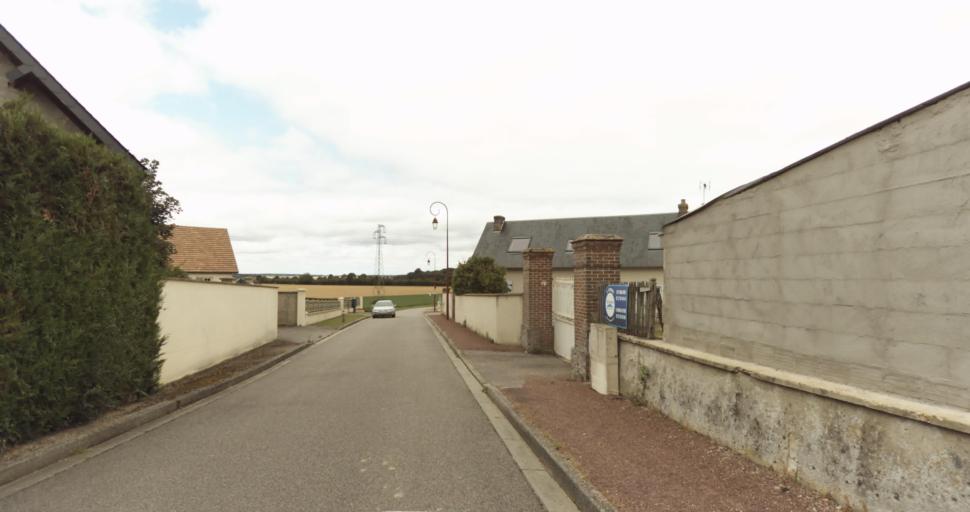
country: FR
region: Haute-Normandie
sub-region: Departement de l'Eure
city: Evreux
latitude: 48.9384
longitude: 1.1936
